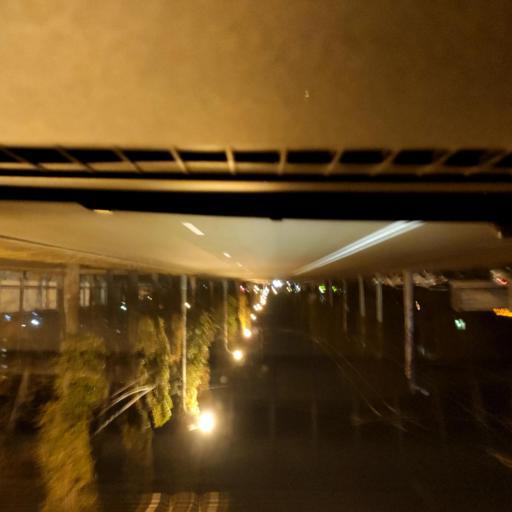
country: RU
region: Voronezj
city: Voronezh
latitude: 51.6557
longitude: 39.1587
